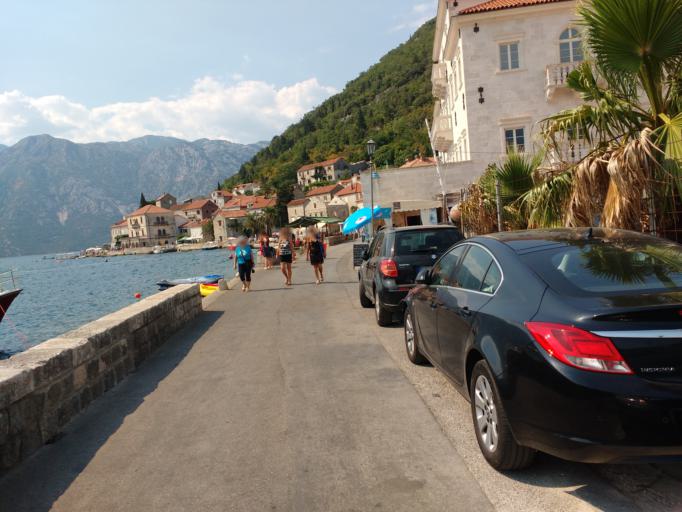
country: ME
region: Kotor
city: Risan
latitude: 42.4867
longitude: 18.6974
